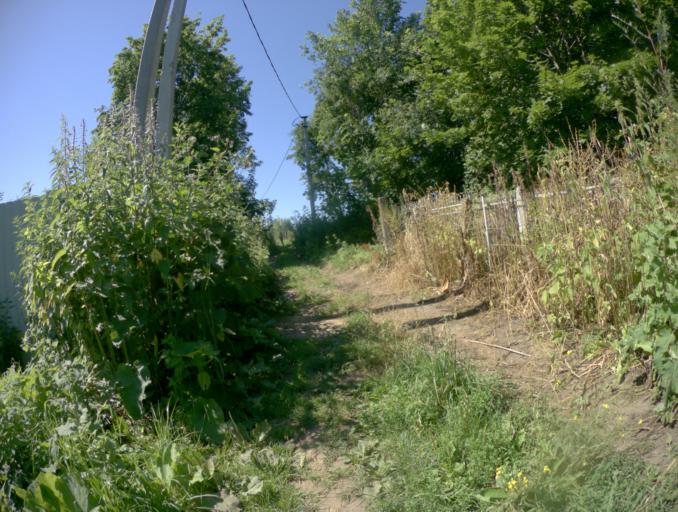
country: RU
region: Nizjnij Novgorod
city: Reshetikha
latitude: 56.1655
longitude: 43.3465
